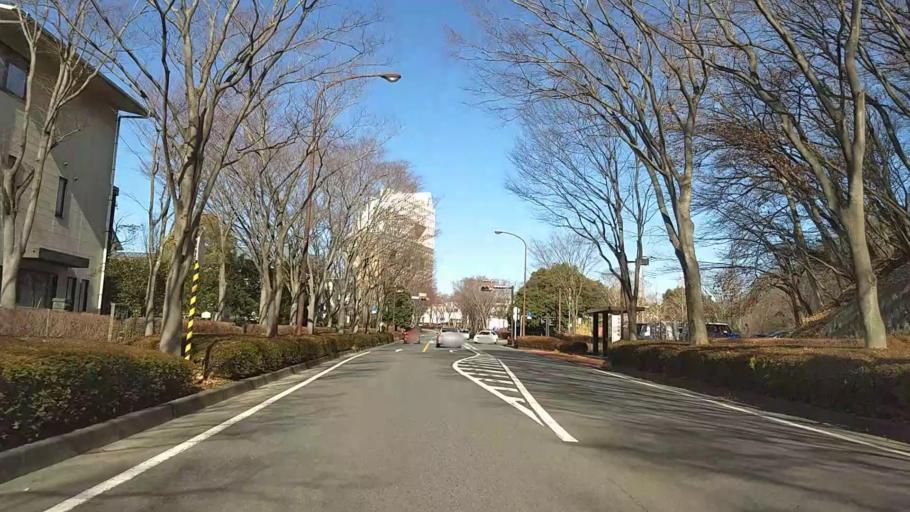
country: JP
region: Kanagawa
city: Atsugi
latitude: 35.4470
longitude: 139.3107
